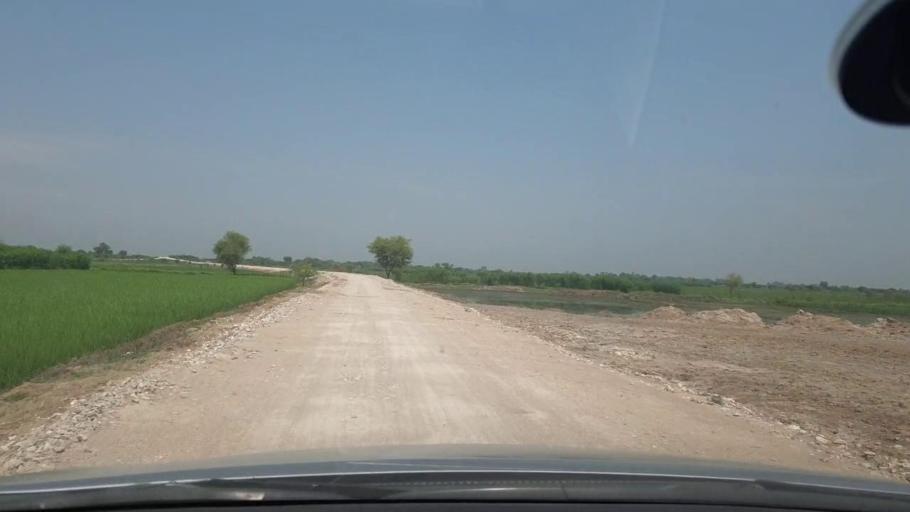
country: PK
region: Balochistan
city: Garhi Khairo
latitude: 28.0569
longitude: 67.9999
